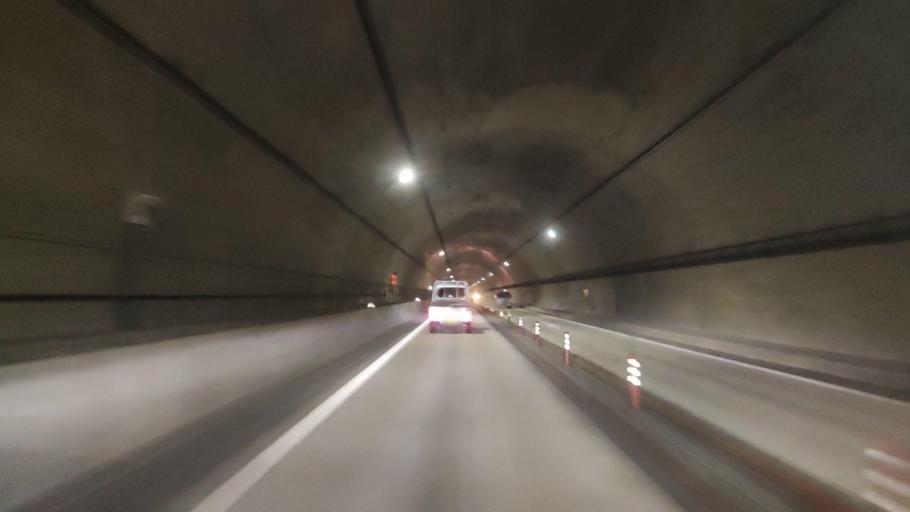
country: JP
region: Wakayama
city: Tanabe
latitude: 33.6183
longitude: 135.4215
